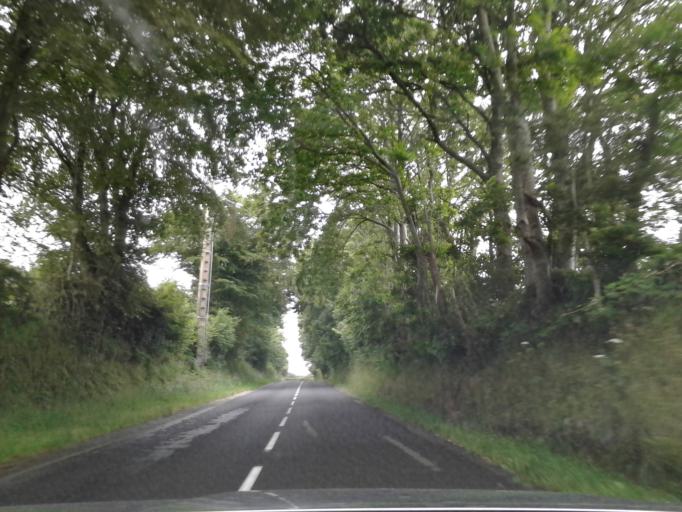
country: FR
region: Lower Normandy
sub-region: Departement de la Manche
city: Beaumont-Hague
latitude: 49.6808
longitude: -1.8448
